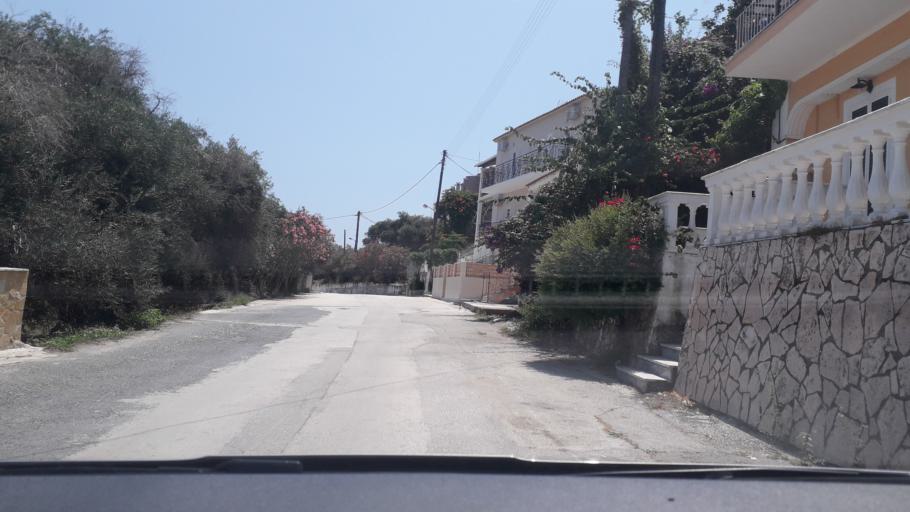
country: GR
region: Ionian Islands
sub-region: Nomos Kerkyras
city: Lefkimmi
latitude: 39.3810
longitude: 20.1146
